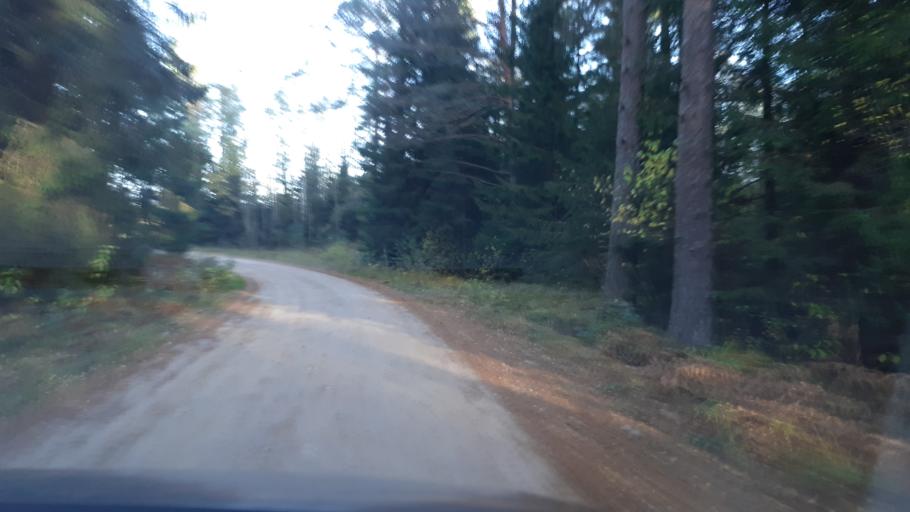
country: LV
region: Kuldigas Rajons
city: Kuldiga
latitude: 56.8601
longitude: 22.1050
